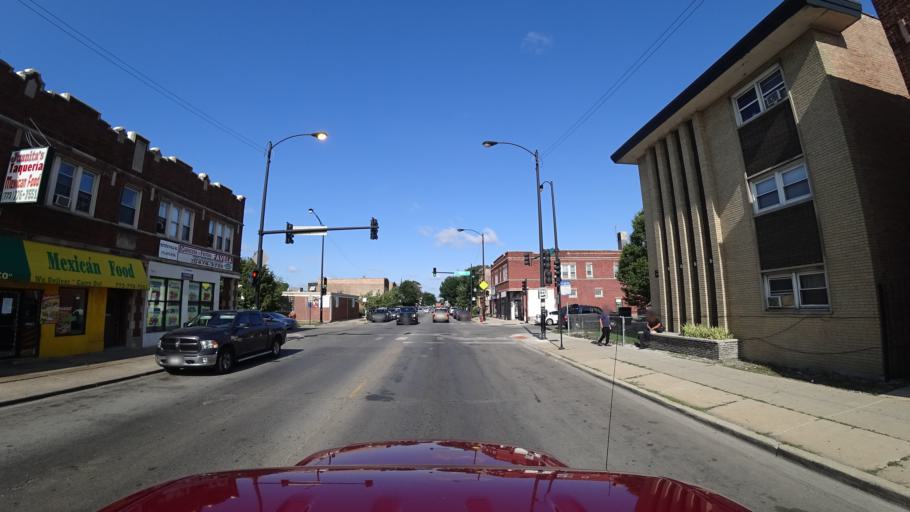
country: US
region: Illinois
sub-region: Cook County
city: Hometown
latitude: 41.7863
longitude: -87.6981
